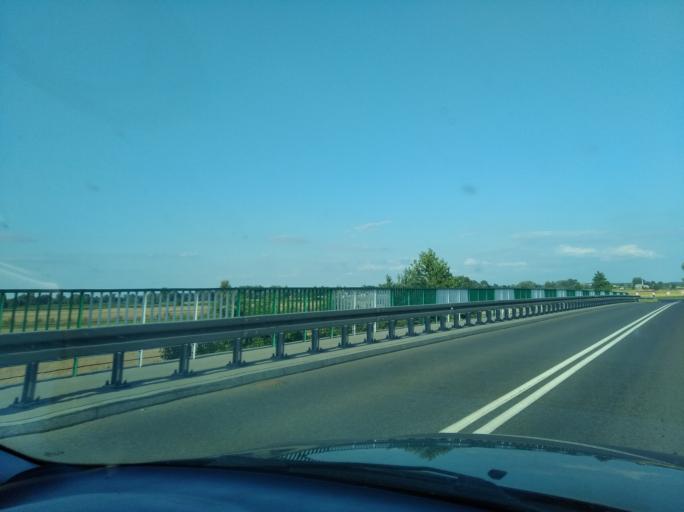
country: PL
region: Subcarpathian Voivodeship
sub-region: Powiat lezajski
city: Stare Miasto
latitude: 50.2911
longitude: 22.4418
